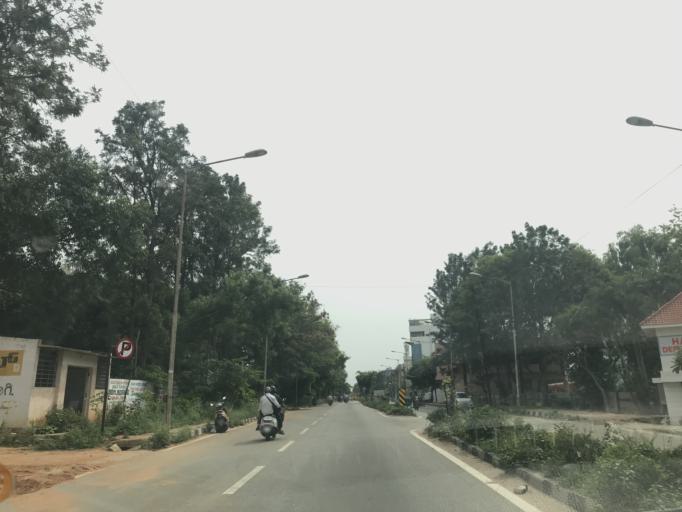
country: IN
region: Karnataka
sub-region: Bangalore Urban
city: Yelahanka
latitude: 13.1238
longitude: 77.6414
